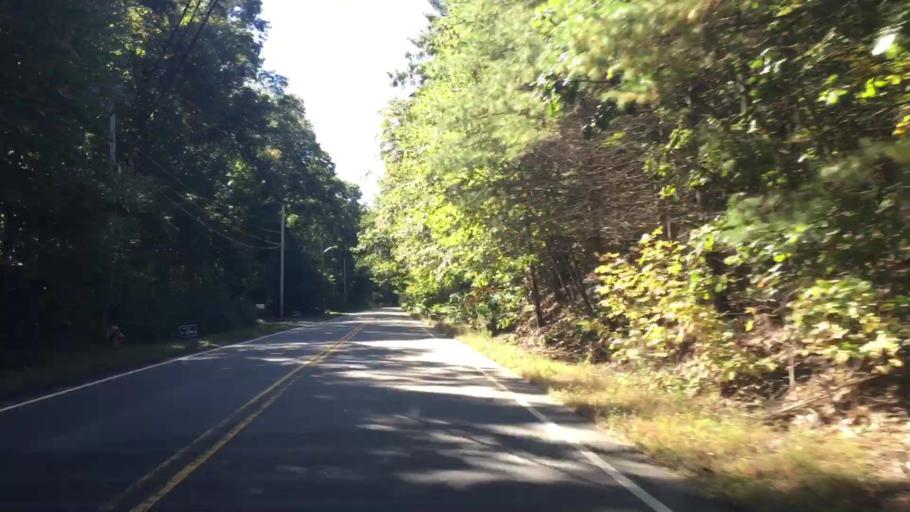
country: US
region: Massachusetts
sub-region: Essex County
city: North Andover
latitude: 42.6877
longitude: -71.0771
